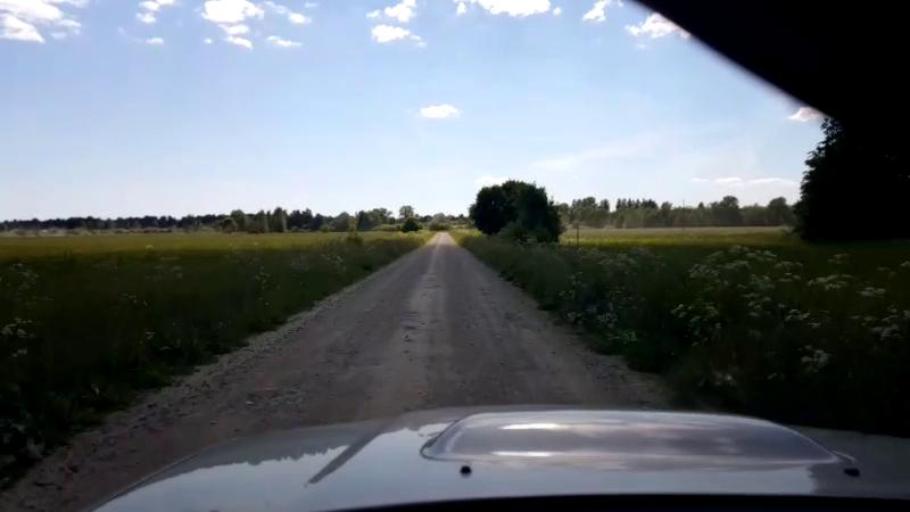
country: EE
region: Paernumaa
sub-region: Sauga vald
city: Sauga
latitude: 58.5134
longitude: 24.5112
